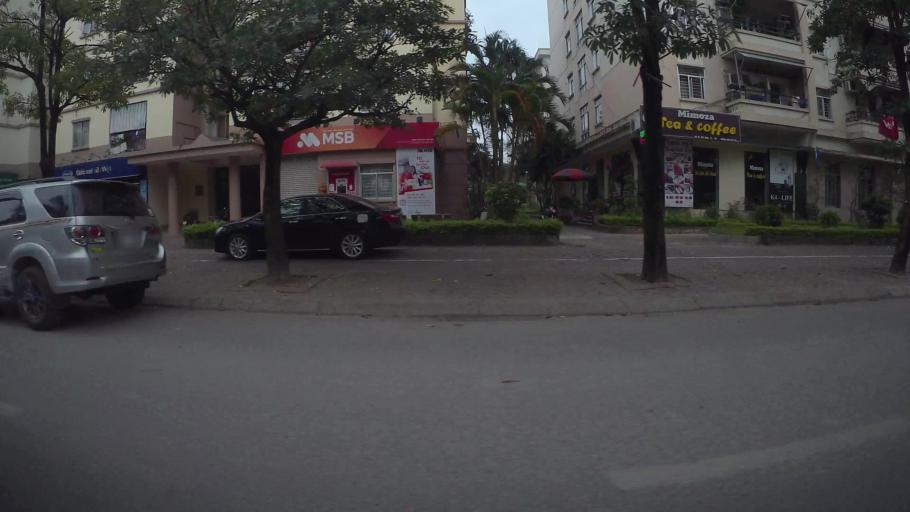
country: VN
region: Ha Noi
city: Trau Quy
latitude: 21.0643
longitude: 105.9080
